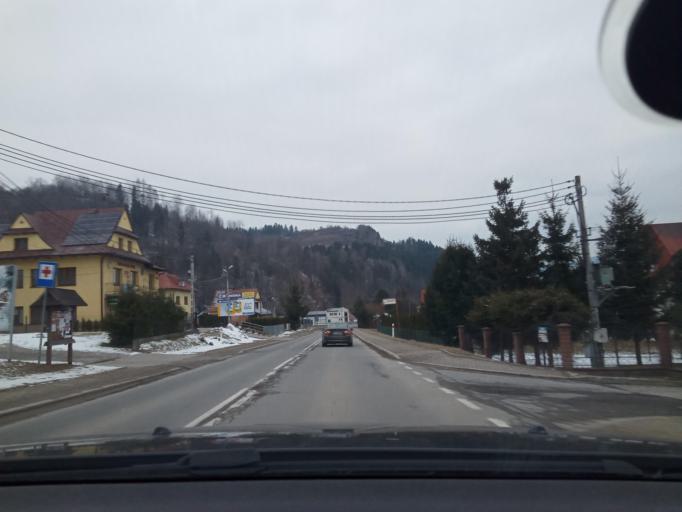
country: PL
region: Lesser Poland Voivodeship
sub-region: Powiat limanowski
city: Mszana Gorna
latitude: 49.6434
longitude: 20.1184
